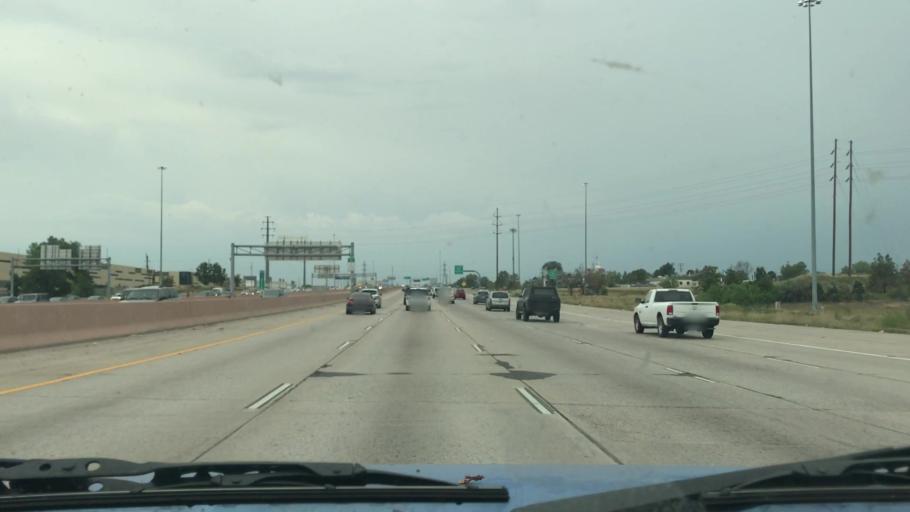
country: US
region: Colorado
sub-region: Adams County
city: Twin Lakes
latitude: 39.8160
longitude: -104.9834
